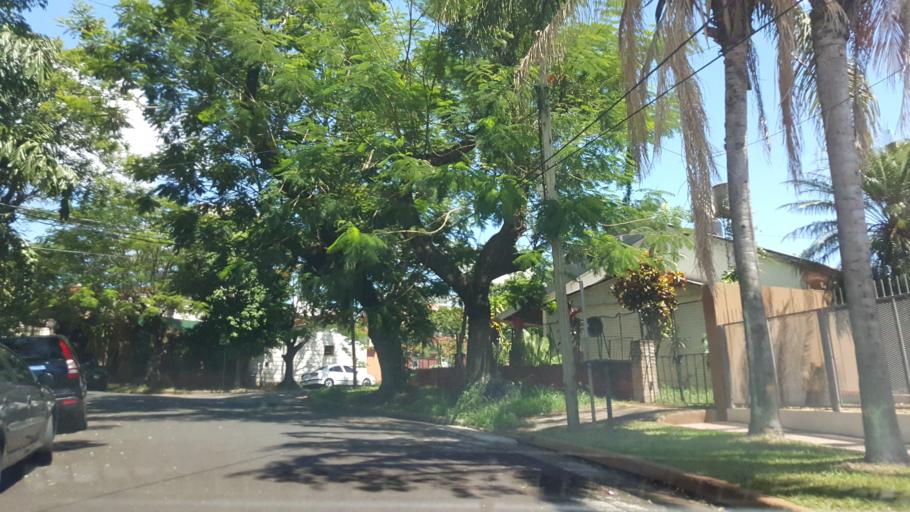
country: AR
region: Misiones
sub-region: Departamento de Capital
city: Posadas
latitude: -27.3535
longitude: -55.8963
